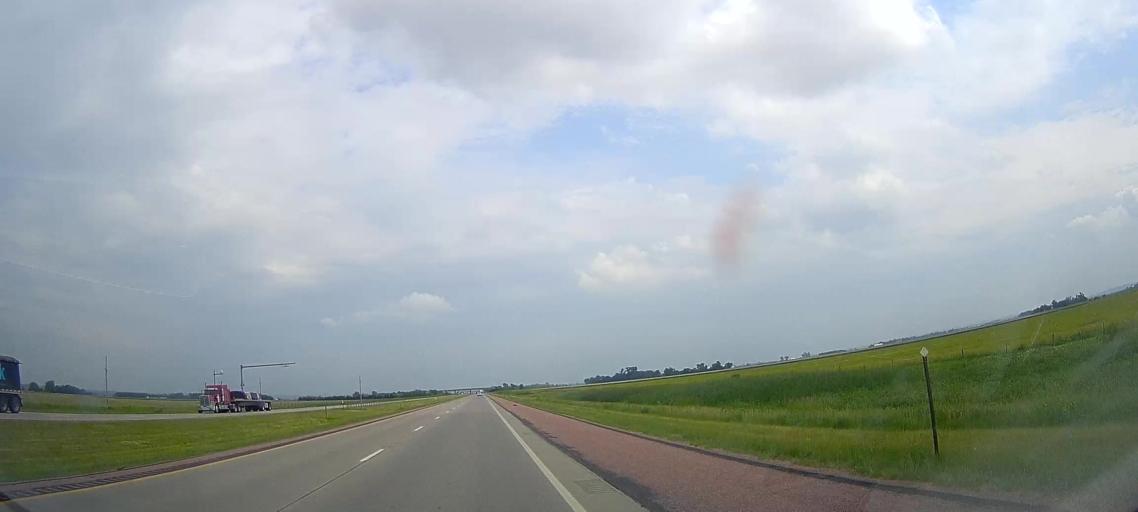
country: US
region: South Dakota
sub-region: Union County
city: Elk Point
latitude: 42.6335
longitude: -96.6145
